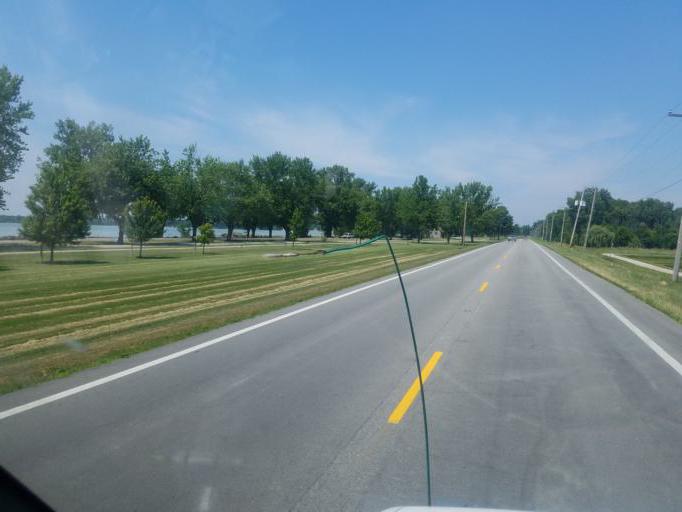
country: US
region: Ohio
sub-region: Auglaize County
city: Saint Marys
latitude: 40.5290
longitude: -84.4191
